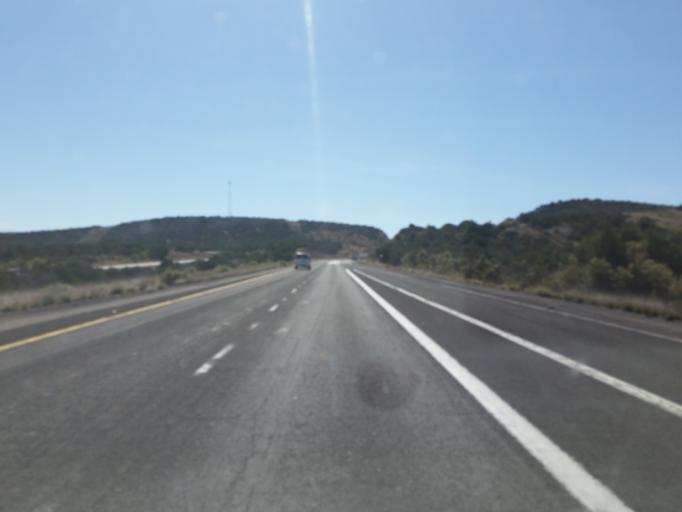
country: US
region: Arizona
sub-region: Mohave County
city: Peach Springs
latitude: 35.1896
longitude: -113.4287
